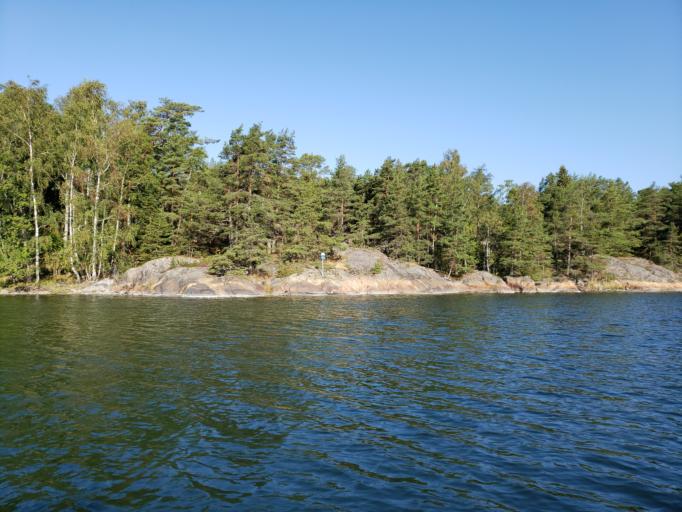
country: FI
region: Varsinais-Suomi
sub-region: Aboland-Turunmaa
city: Dragsfjaerd
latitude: 59.9142
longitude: 22.3793
